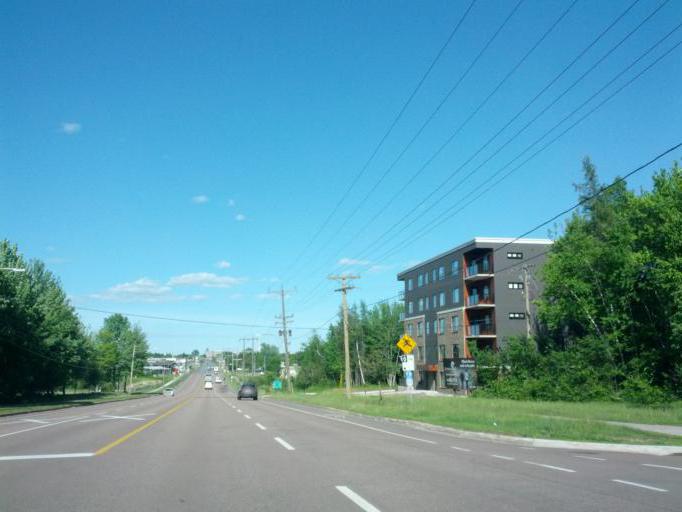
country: CA
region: New Brunswick
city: Moncton
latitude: 46.0836
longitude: -64.8180
